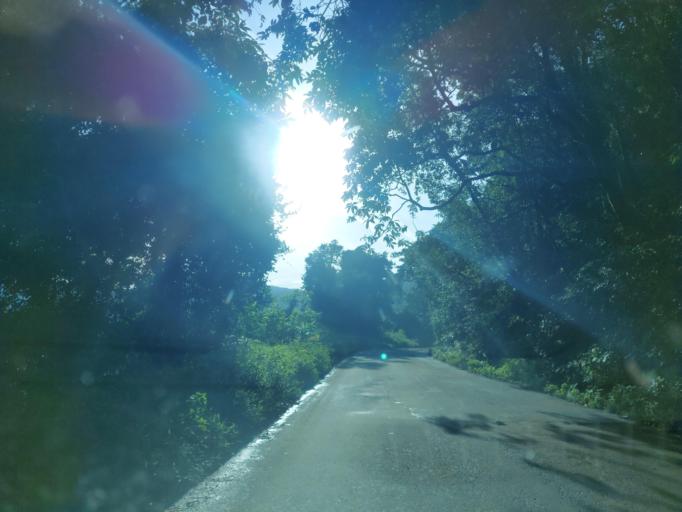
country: IN
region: Maharashtra
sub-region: Sindhudurg
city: Savantvadi
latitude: 15.9352
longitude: 73.9741
